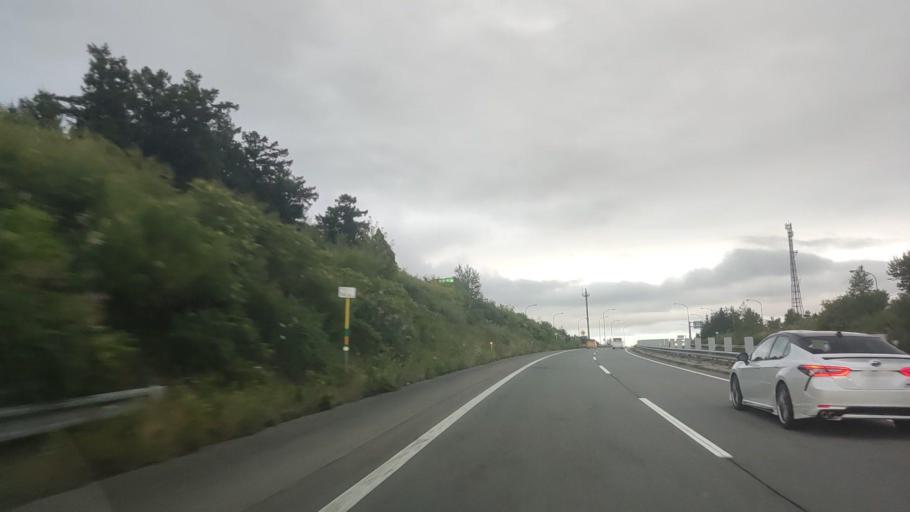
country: JP
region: Hokkaido
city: Nanae
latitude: 41.8967
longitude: 140.7083
